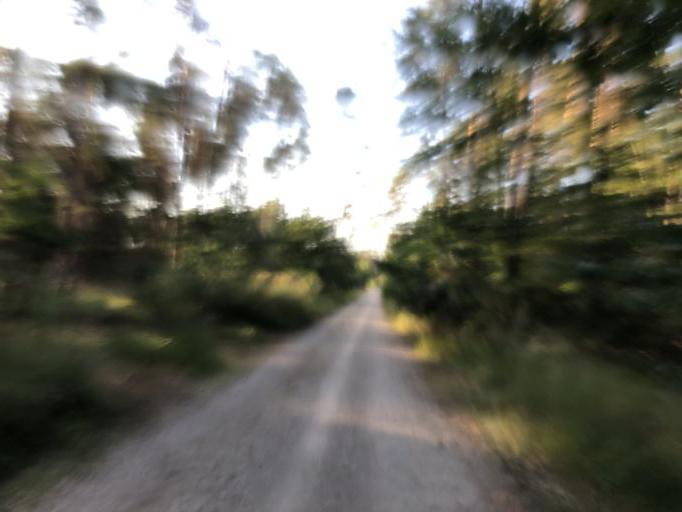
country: DE
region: Bavaria
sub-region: Regierungsbezirk Mittelfranken
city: Uttenreuth
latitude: 49.5778
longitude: 11.0732
